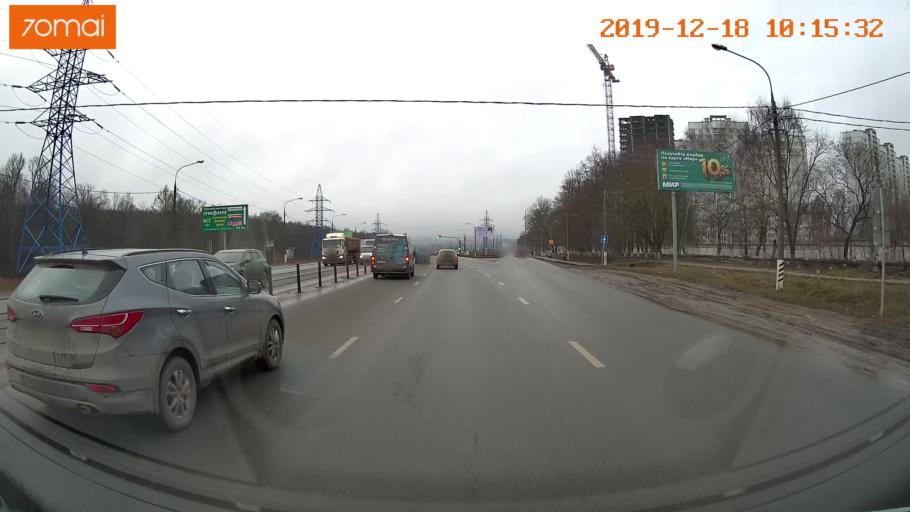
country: RU
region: Moskovskaya
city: Dubrovitsy
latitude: 55.4105
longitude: 37.4790
